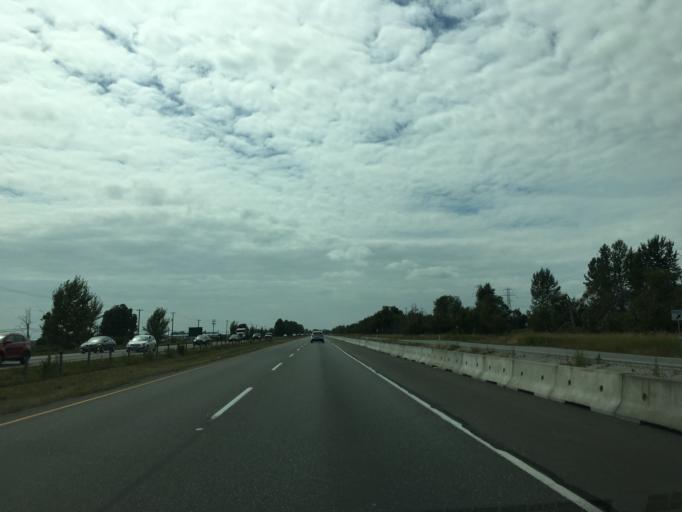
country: CA
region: British Columbia
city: Delta
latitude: 49.0905
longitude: -122.9802
